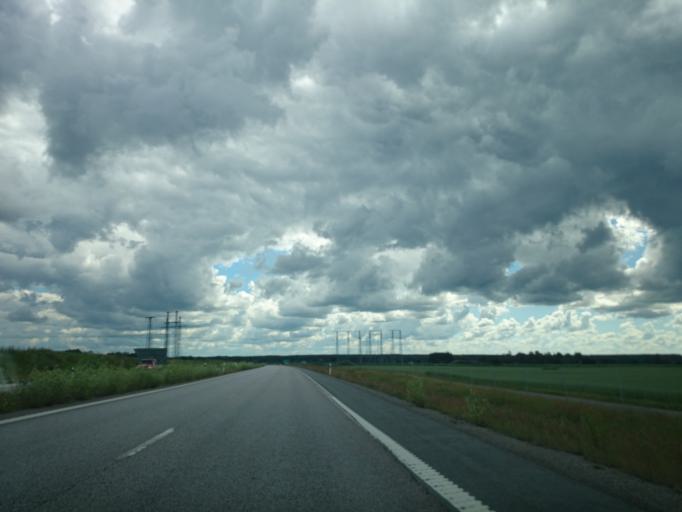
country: SE
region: Uppsala
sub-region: Tierps Kommun
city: Tierp
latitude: 60.3354
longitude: 17.4930
